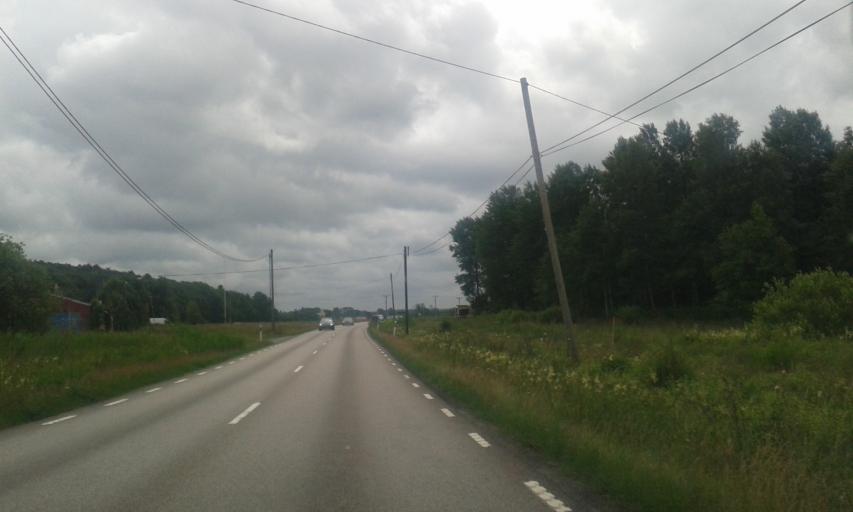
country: SE
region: Vaestra Goetaland
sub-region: Kungalvs Kommun
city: Kode
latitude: 57.8875
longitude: 11.8879
